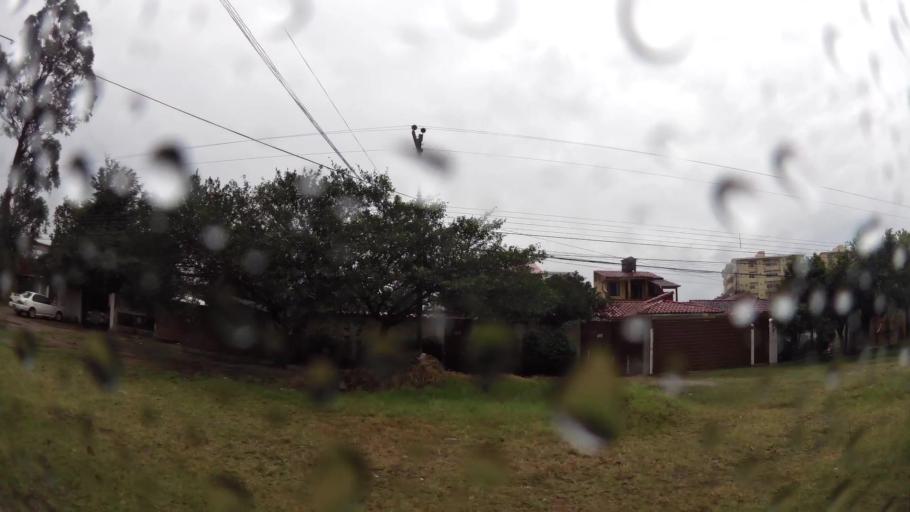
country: BO
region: Santa Cruz
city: Santa Cruz de la Sierra
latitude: -17.8049
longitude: -63.2215
